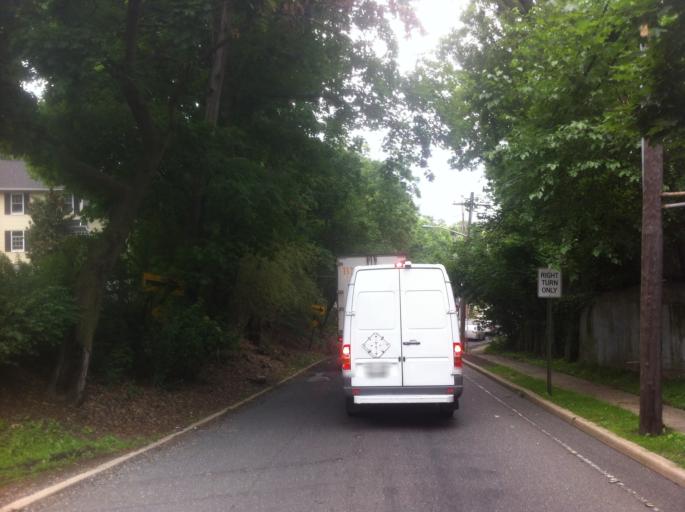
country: US
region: New York
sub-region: Nassau County
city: Roslyn Estates
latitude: 40.7994
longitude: -73.6581
